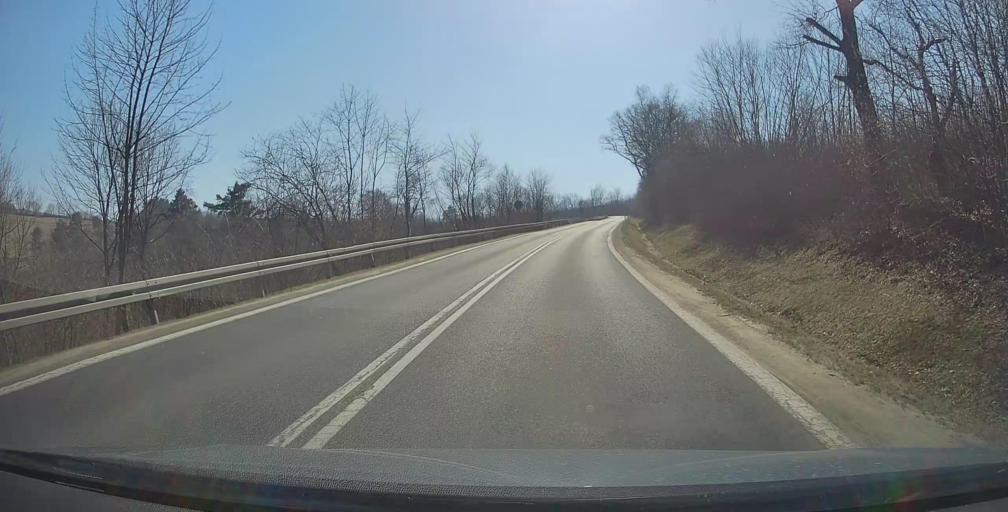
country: PL
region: Subcarpathian Voivodeship
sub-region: Powiat przemyski
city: Bircza
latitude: 49.6528
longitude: 22.4226
